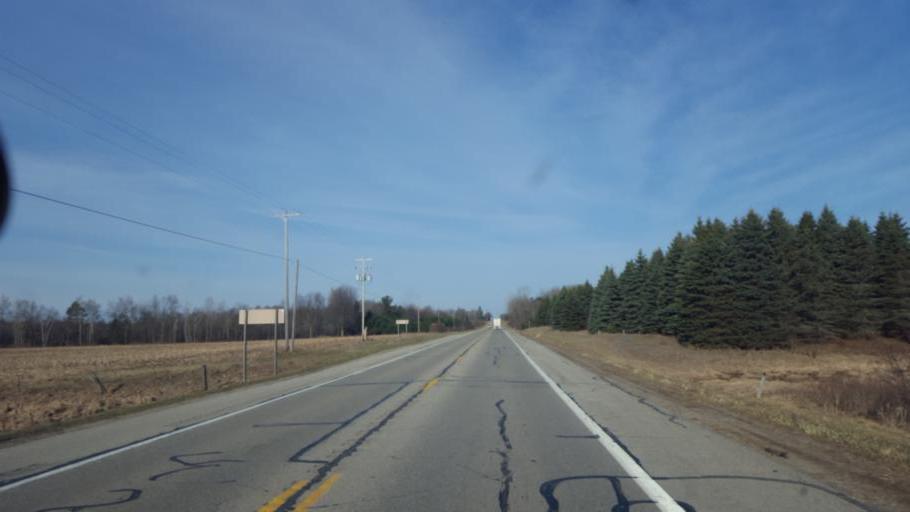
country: US
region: Michigan
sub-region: Montcalm County
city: Lakeview
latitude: 43.4301
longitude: -85.1649
